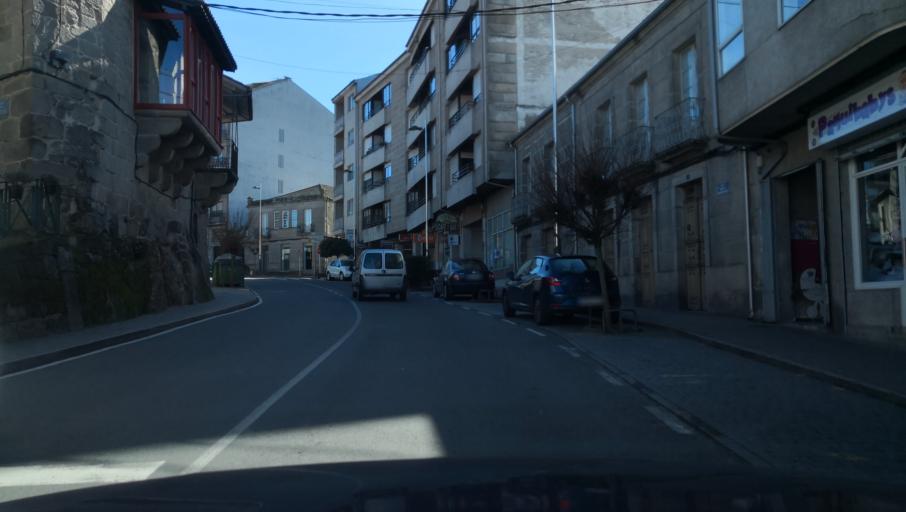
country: ES
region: Galicia
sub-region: Provincia de Ourense
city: Allariz
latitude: 42.1883
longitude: -7.8033
